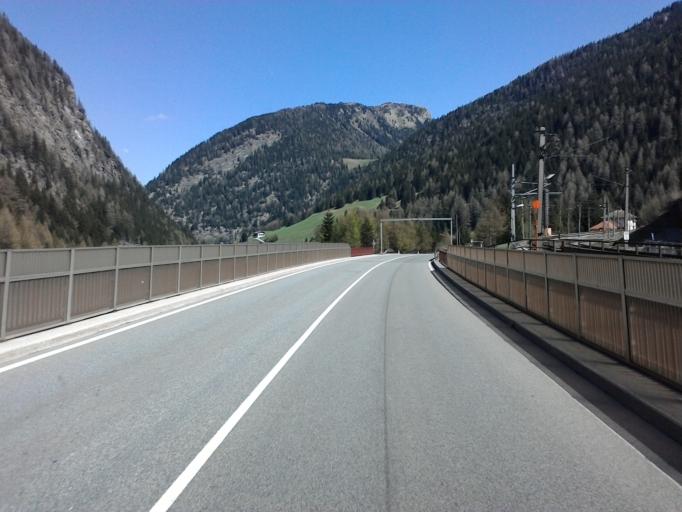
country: AT
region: Tyrol
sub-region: Politischer Bezirk Innsbruck Land
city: Gries am Brenner
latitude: 47.0133
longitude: 11.5069
